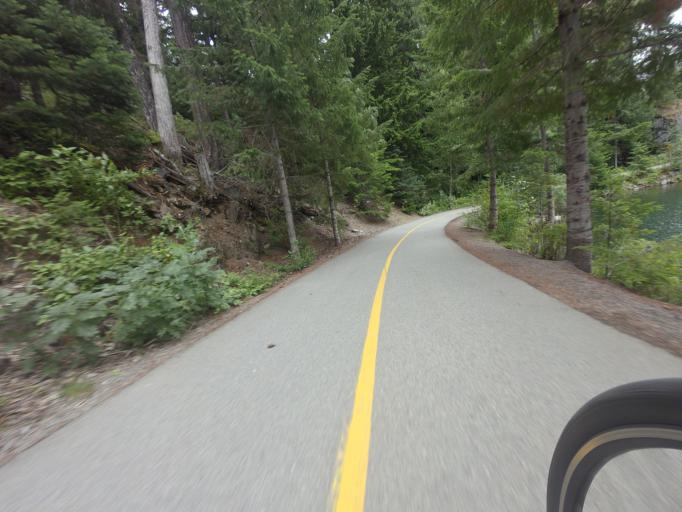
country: CA
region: British Columbia
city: Whistler
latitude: 50.1014
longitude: -122.9929
